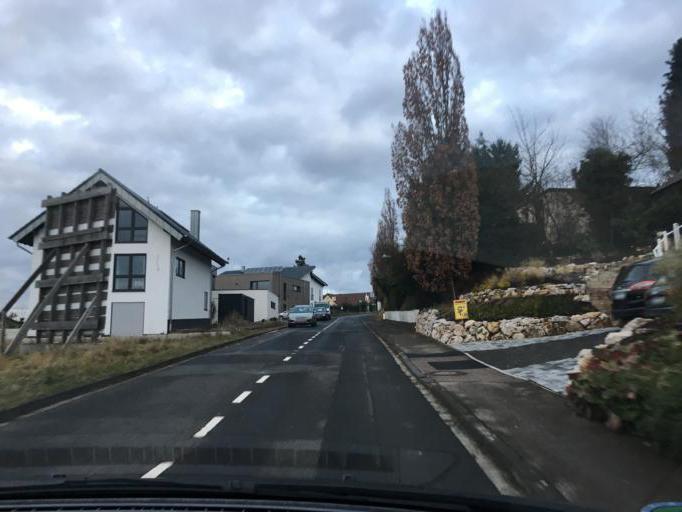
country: DE
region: North Rhine-Westphalia
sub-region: Regierungsbezirk Koln
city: Mechernich
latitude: 50.6080
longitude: 6.6493
